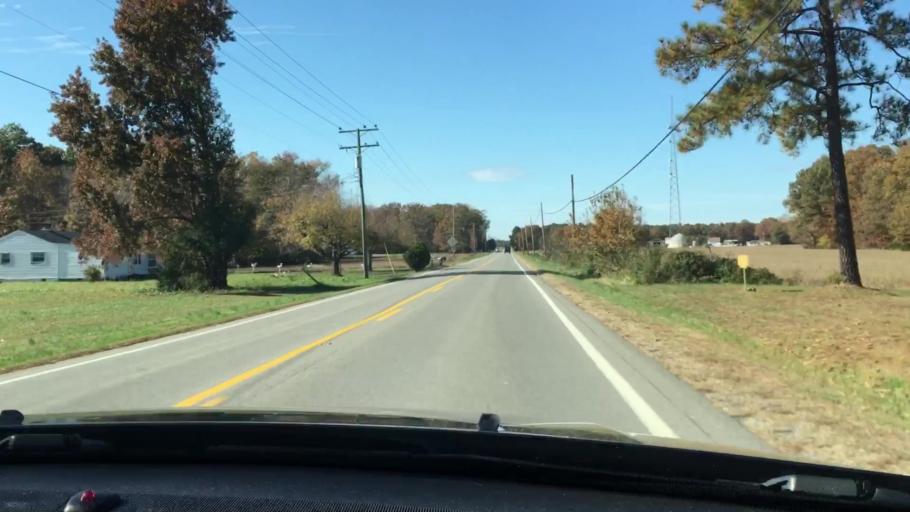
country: US
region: Virginia
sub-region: King William County
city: Central Garage
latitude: 37.7185
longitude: -77.0753
